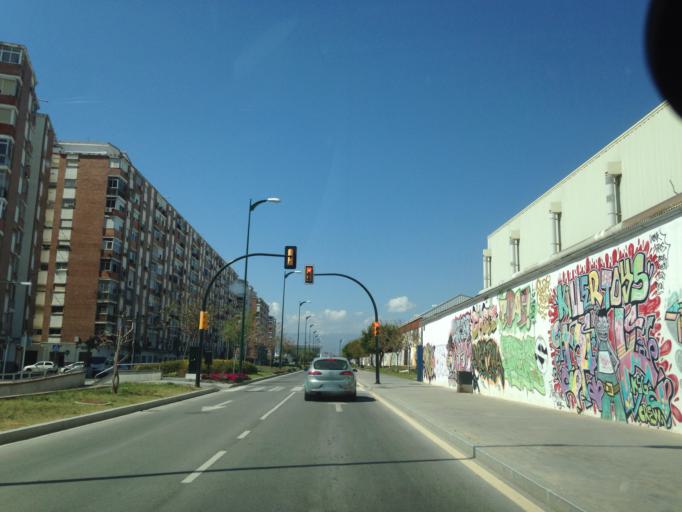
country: ES
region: Andalusia
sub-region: Provincia de Malaga
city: Malaga
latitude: 36.7034
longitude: -4.4502
